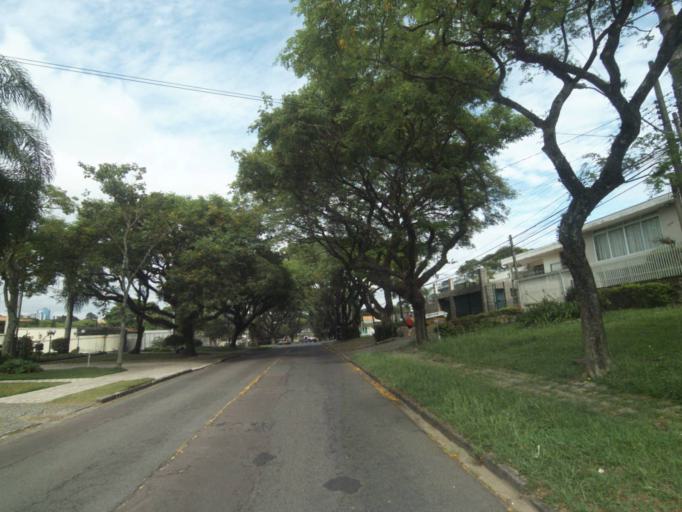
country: BR
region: Parana
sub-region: Curitiba
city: Curitiba
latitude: -25.4250
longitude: -49.2337
